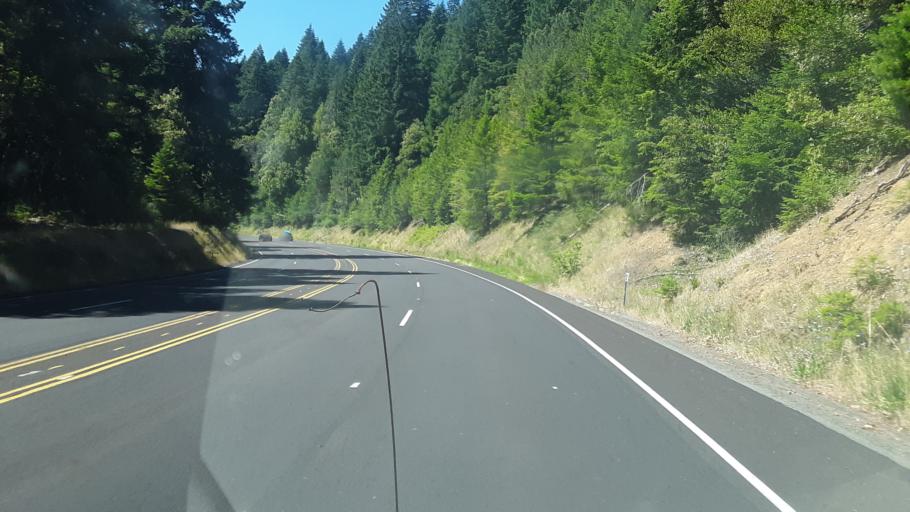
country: US
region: Oregon
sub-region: Josephine County
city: Cave Junction
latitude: 41.9134
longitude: -123.7697
